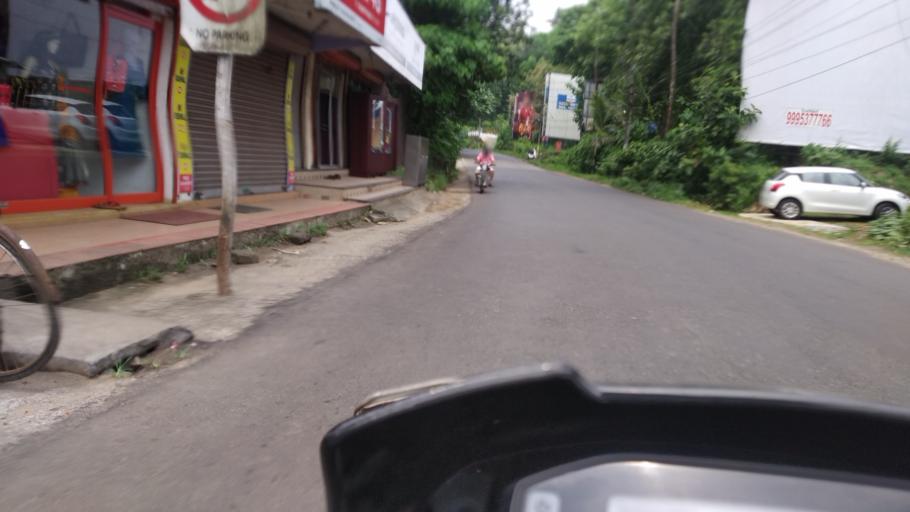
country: IN
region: Kerala
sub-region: Ernakulam
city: Perumpavur
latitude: 10.1015
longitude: 76.5419
